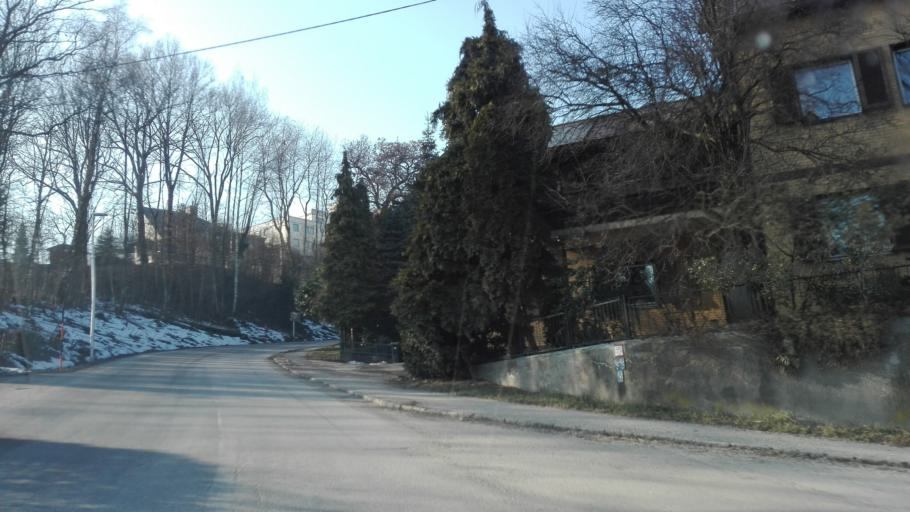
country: AT
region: Upper Austria
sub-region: Politischer Bezirk Linz-Land
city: Leonding
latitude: 48.2792
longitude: 14.2731
